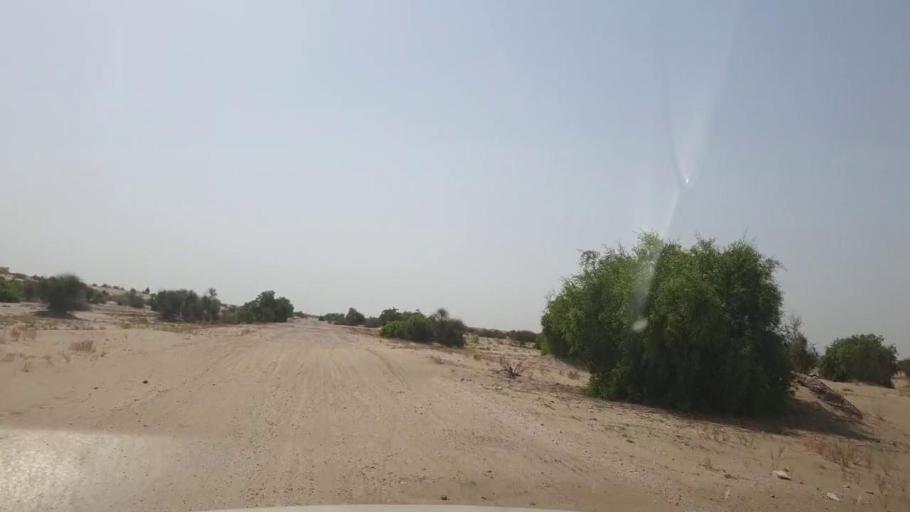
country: PK
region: Sindh
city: Rohri
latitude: 27.4508
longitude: 69.2291
